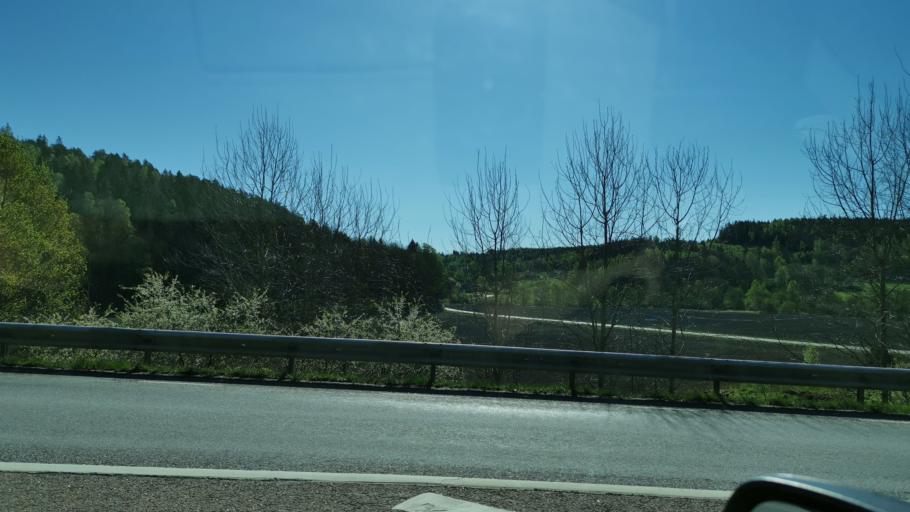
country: SE
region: Vaestra Goetaland
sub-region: Uddevalla Kommun
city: Ljungskile
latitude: 58.2852
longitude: 11.8922
